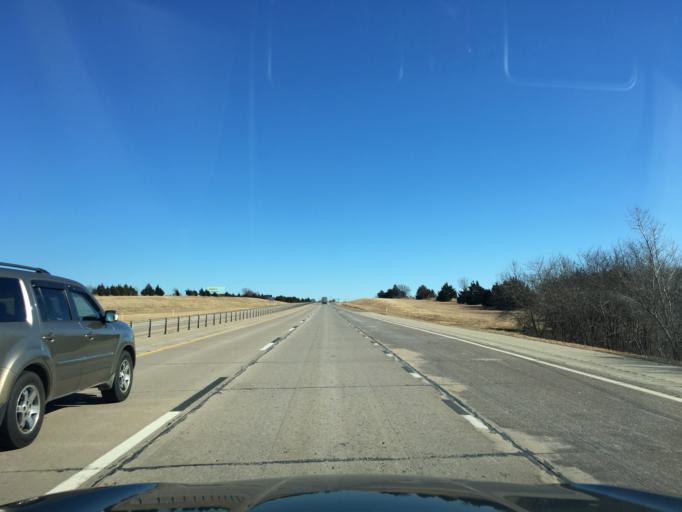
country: US
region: Oklahoma
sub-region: Pawnee County
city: Pawnee
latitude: 36.2397
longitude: -96.9394
